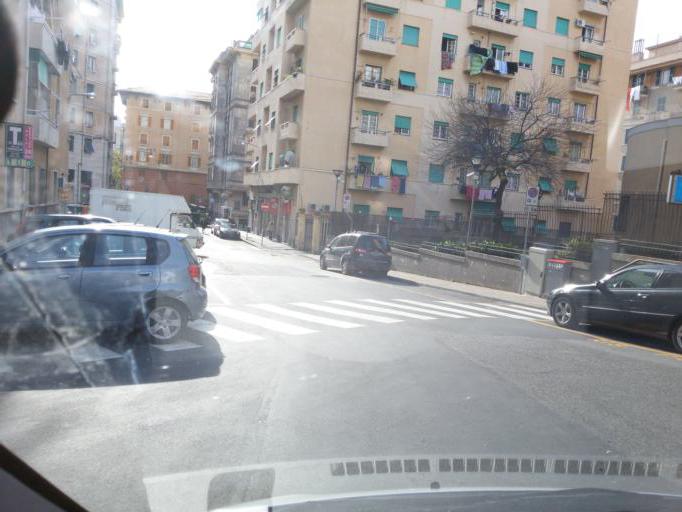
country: IT
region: Liguria
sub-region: Provincia di Genova
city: Genoa
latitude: 44.4081
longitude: 8.9640
